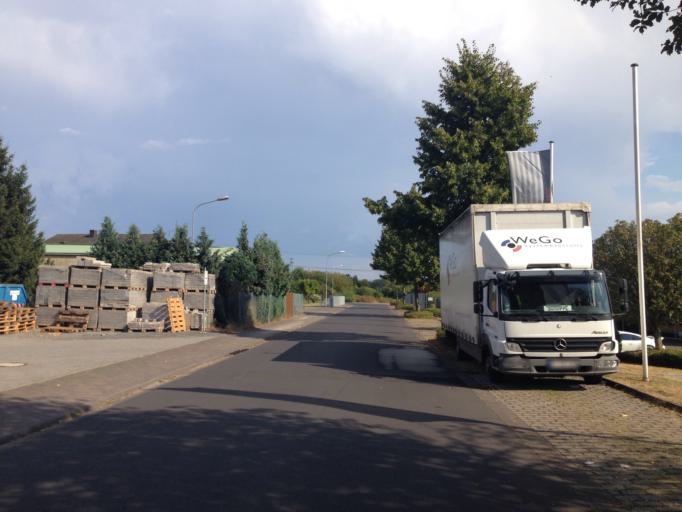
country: DE
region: Hesse
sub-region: Regierungsbezirk Giessen
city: Giessen
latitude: 50.6179
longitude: 8.6616
